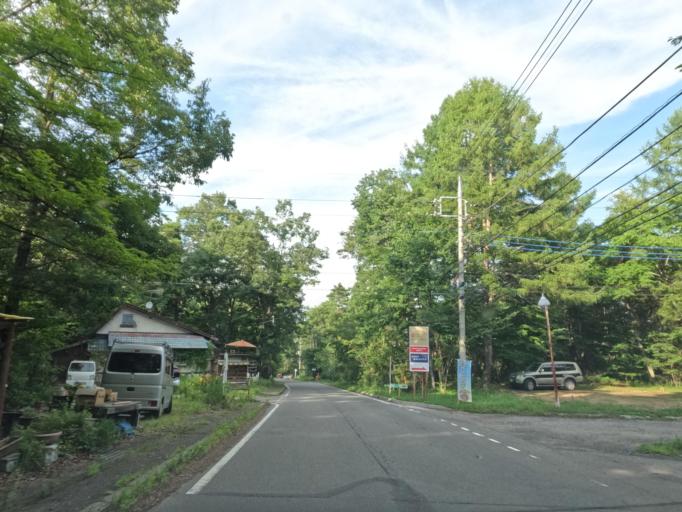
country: JP
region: Nagano
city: Komoro
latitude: 36.4671
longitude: 138.5617
